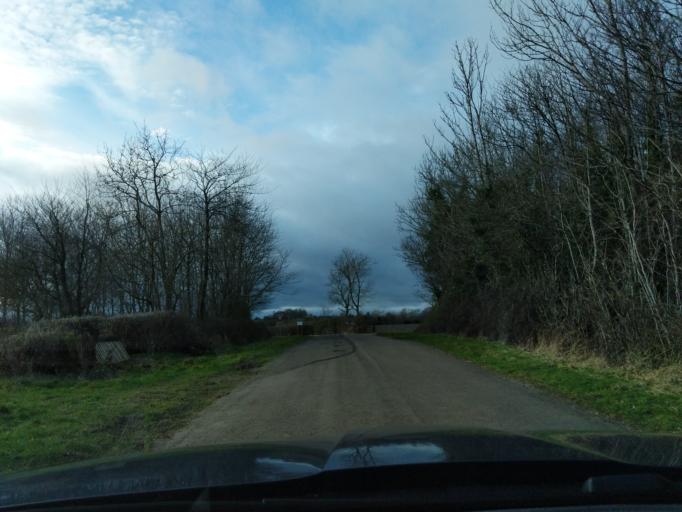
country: GB
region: England
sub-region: Northumberland
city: Ancroft
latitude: 55.6855
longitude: -1.9714
